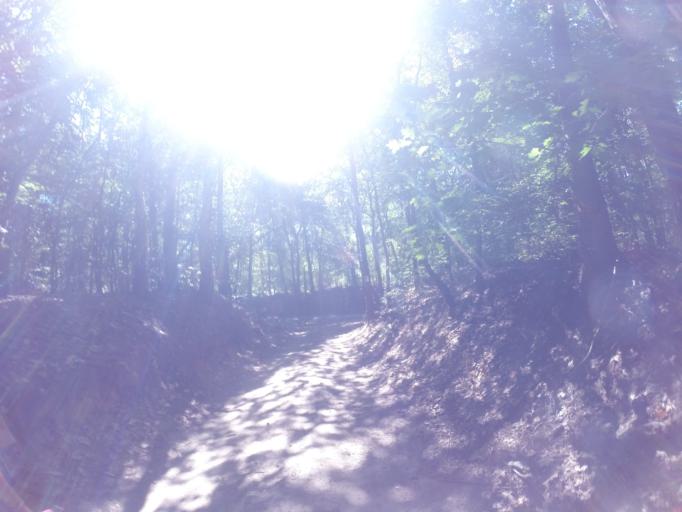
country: NL
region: Gelderland
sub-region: Gemeente Lochem
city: Lochem
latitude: 52.1378
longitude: 6.4185
